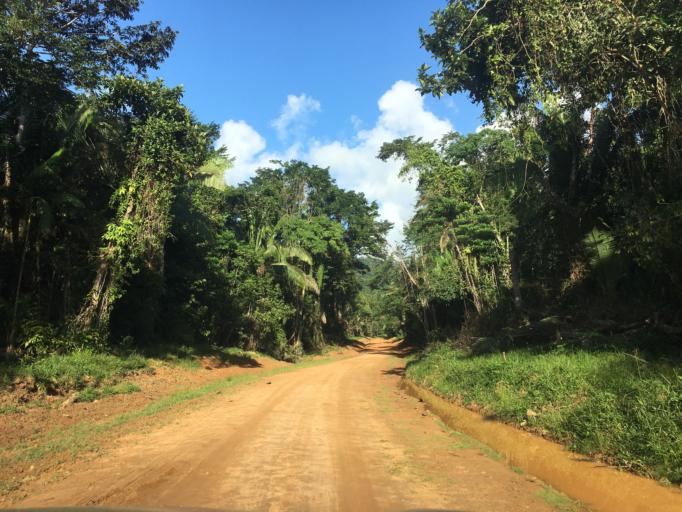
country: BZ
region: Stann Creek
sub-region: Dangriga
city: Dangriga
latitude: 16.7890
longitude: -88.4467
